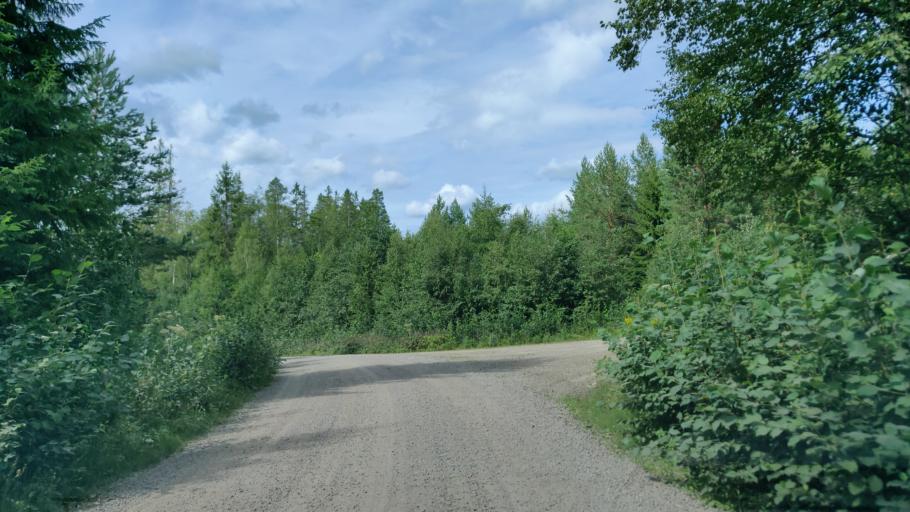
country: SE
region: Vaermland
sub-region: Hagfors Kommun
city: Hagfors
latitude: 60.0093
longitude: 13.7096
